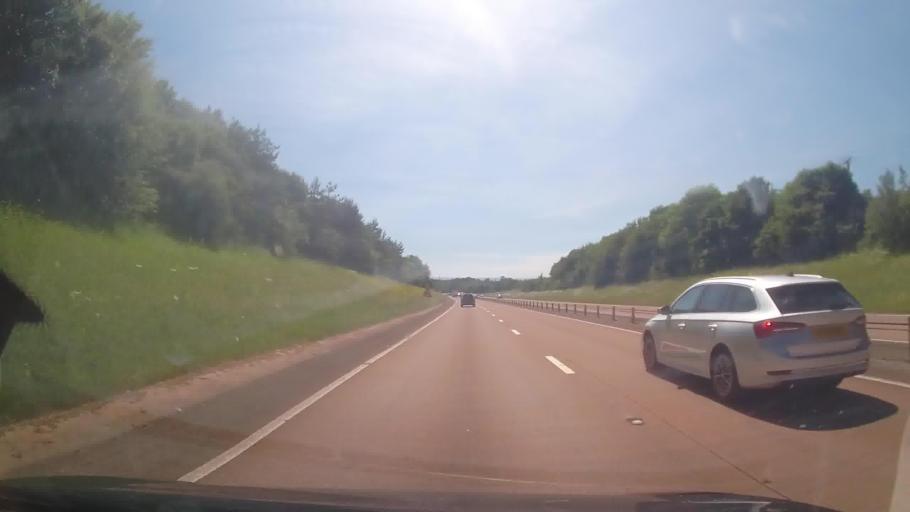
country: GB
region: England
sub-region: Devon
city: Newton Poppleford
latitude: 50.7463
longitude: -3.3527
